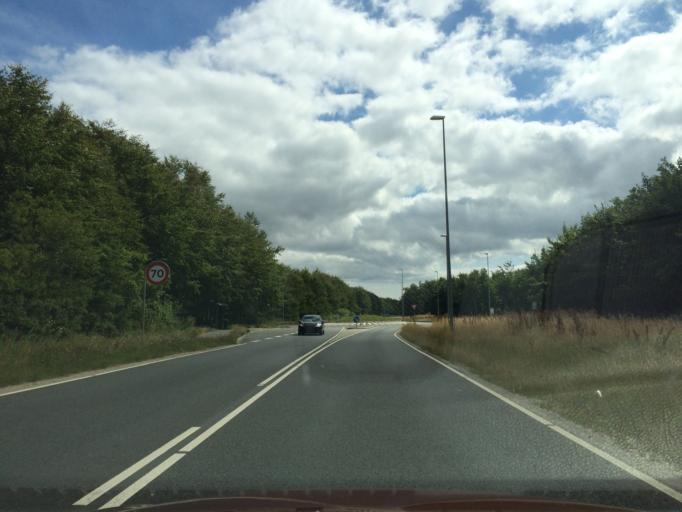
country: DK
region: Central Jutland
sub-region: Silkeborg Kommune
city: Silkeborg
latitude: 56.1957
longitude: 9.6007
